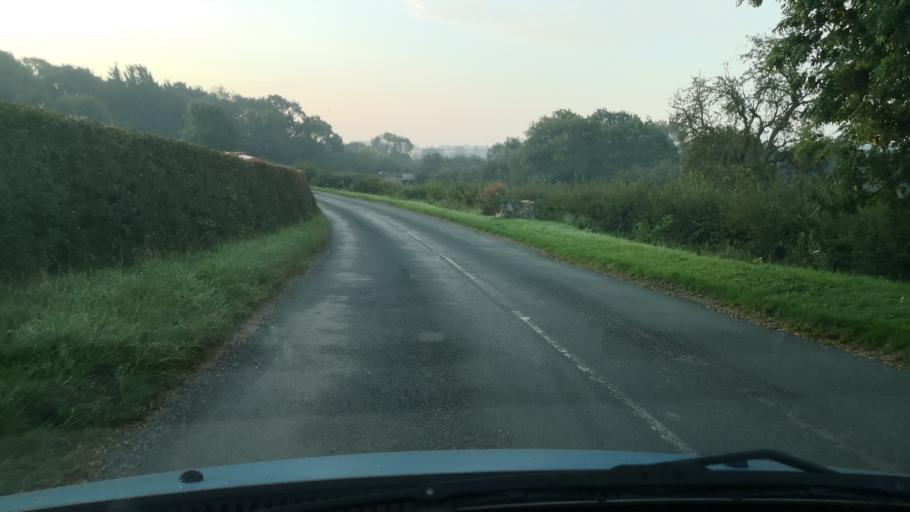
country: GB
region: England
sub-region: Doncaster
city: Norton
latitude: 53.6426
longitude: -1.2018
